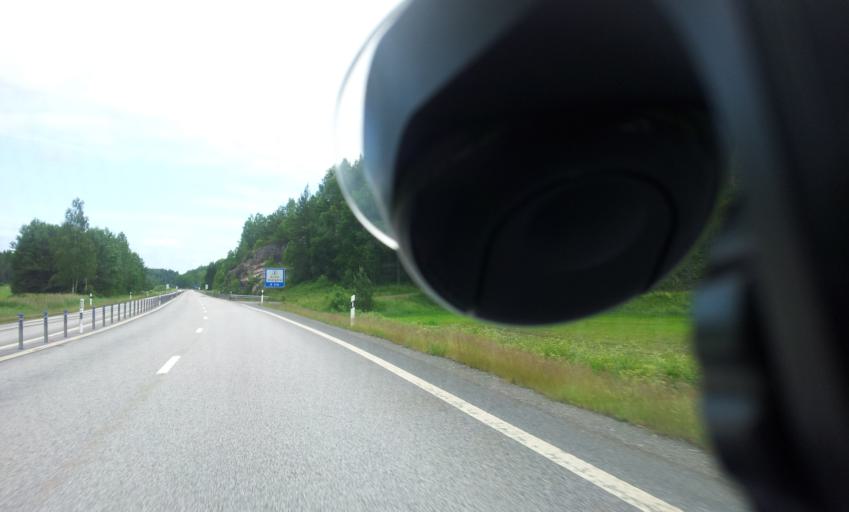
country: SE
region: OEstergoetland
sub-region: Valdemarsviks Kommun
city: Valdemarsvik
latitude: 58.2019
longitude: 16.5561
